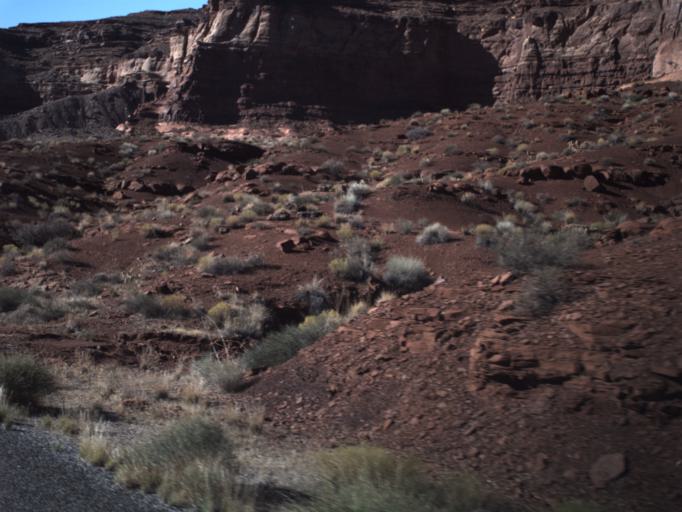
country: US
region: Utah
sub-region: San Juan County
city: Blanding
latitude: 37.9078
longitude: -110.4006
